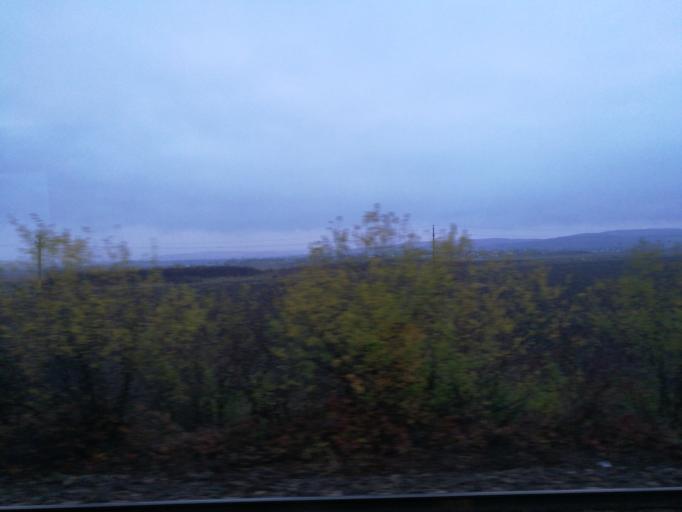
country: RO
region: Prahova
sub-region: Comuna Valea Calugareasca
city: Rachieri
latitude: 44.9446
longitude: 26.1300
